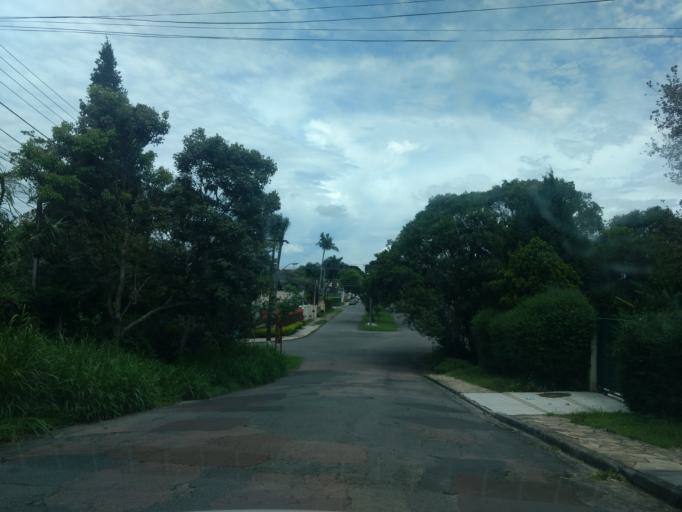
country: BR
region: Parana
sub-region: Pinhais
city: Pinhais
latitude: -25.4180
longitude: -49.2269
